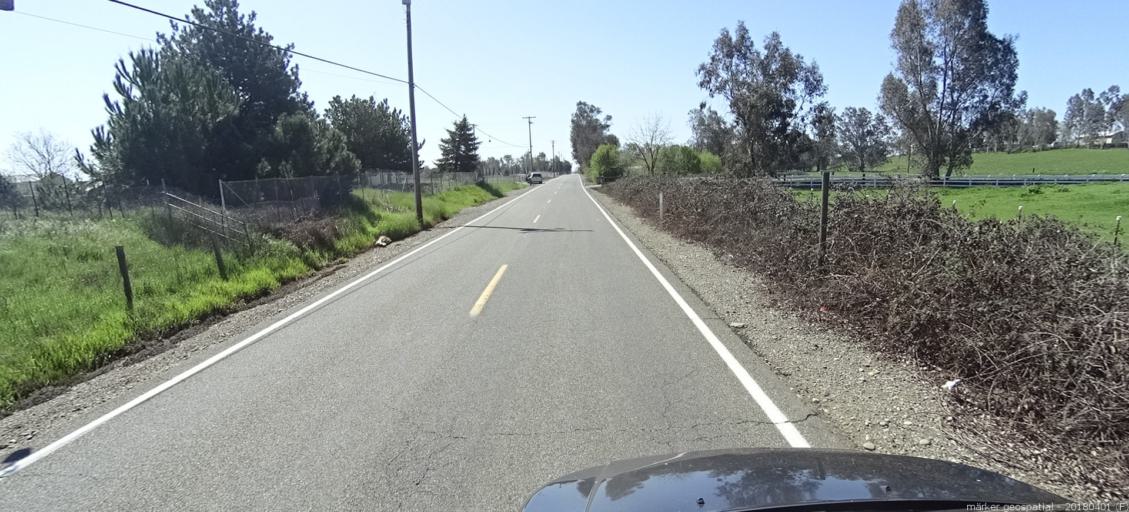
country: US
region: California
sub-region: Sacramento County
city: Herald
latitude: 38.3481
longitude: -121.2237
